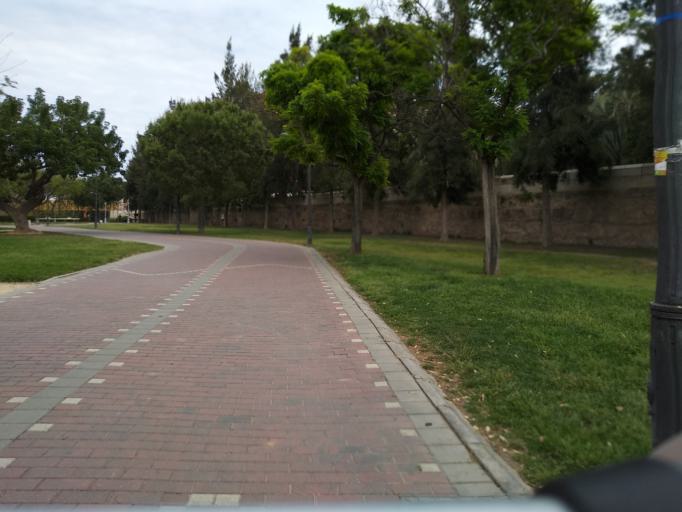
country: ES
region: Valencia
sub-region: Provincia de Valencia
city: Mislata
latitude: 39.4735
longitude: -0.4045
